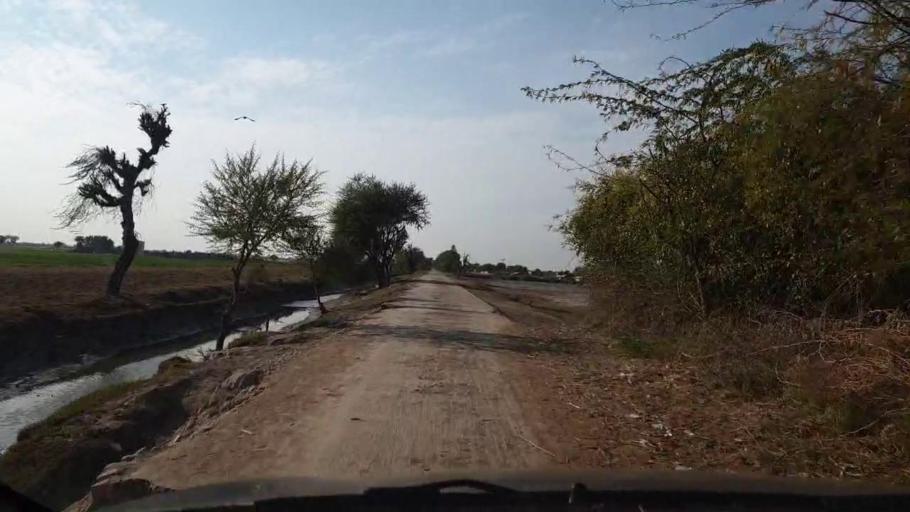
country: PK
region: Sindh
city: Sinjhoro
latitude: 25.9765
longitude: 68.8215
